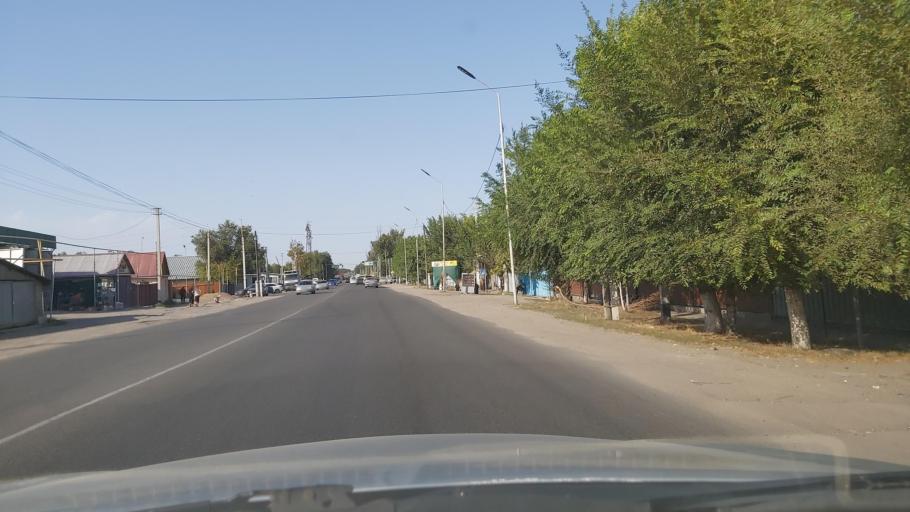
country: KZ
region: Almaty Oblysy
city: Energeticheskiy
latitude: 43.4782
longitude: 77.0319
